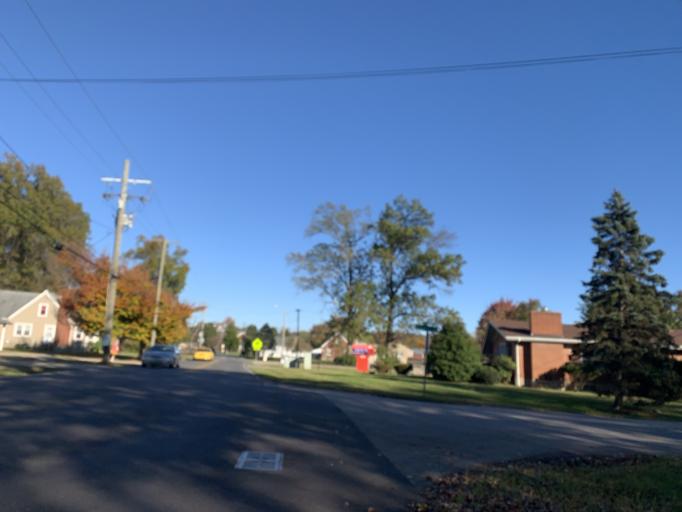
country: US
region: Kentucky
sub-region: Jefferson County
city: Saint Dennis
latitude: 38.1672
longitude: -85.8388
